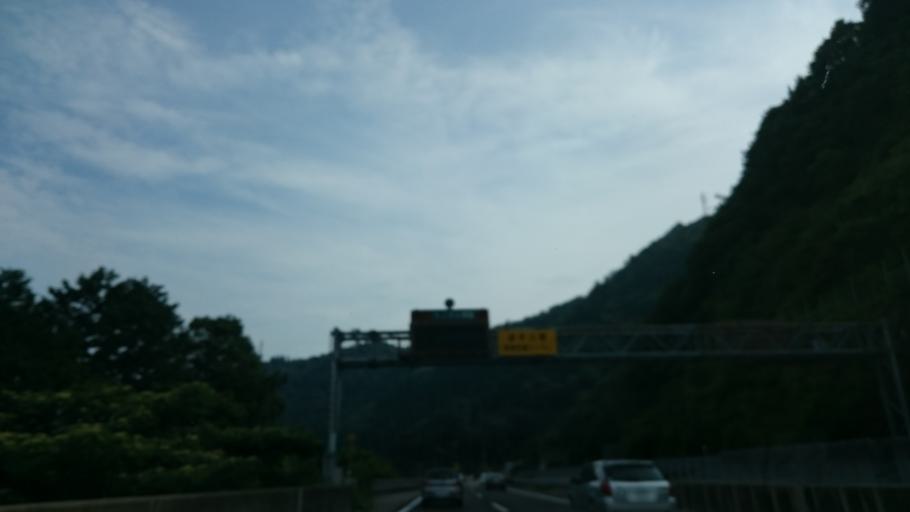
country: JP
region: Gifu
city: Gujo
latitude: 35.7432
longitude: 136.9449
